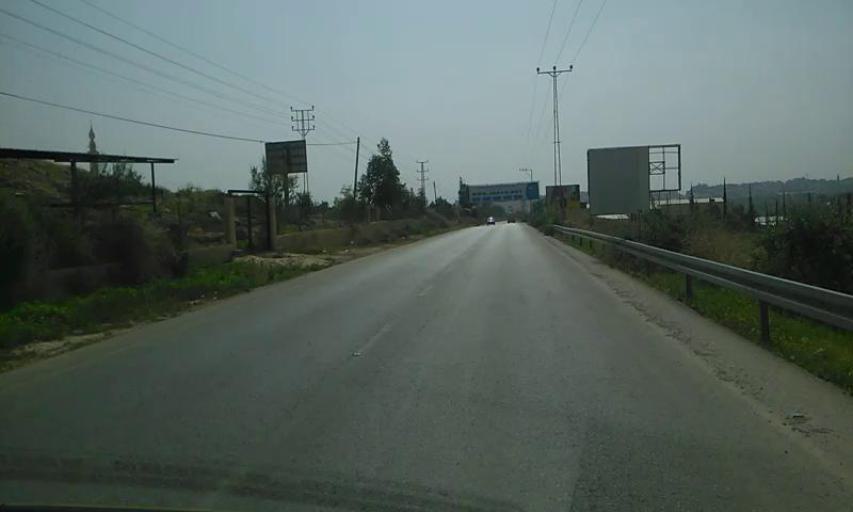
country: PS
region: West Bank
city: An Nuway`imah
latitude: 31.8903
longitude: 35.4317
